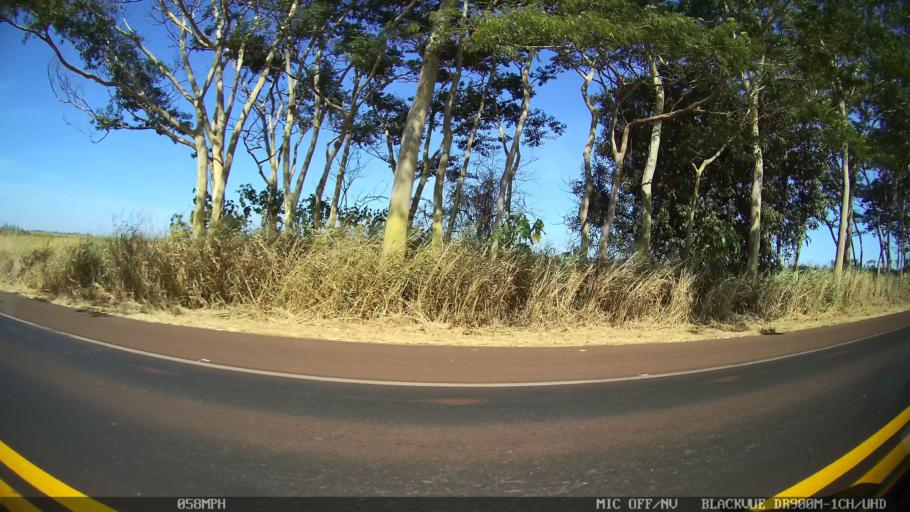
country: BR
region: Sao Paulo
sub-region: Barretos
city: Barretos
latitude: -20.4849
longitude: -48.5114
